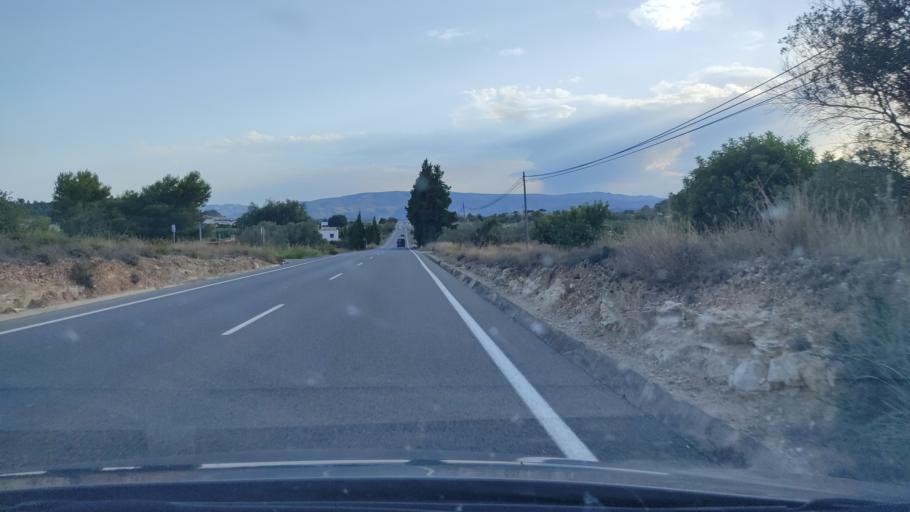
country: ES
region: Valencia
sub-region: Provincia de Valencia
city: Monserrat
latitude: 39.3672
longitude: -0.5804
